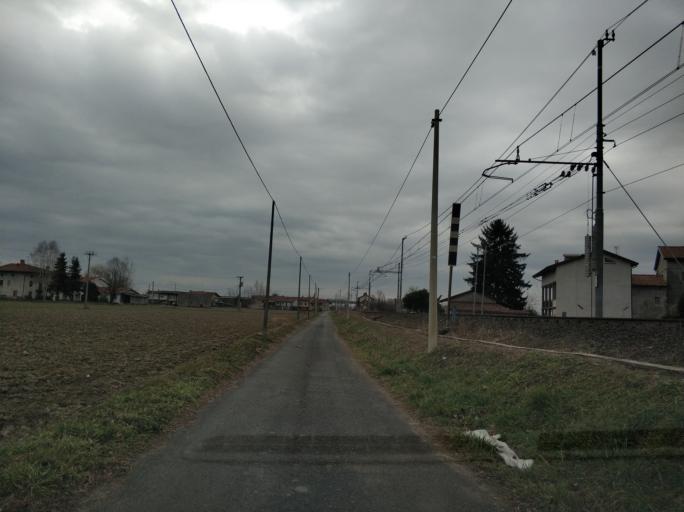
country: IT
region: Piedmont
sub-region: Provincia di Torino
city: Ivrea
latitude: 45.4485
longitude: 7.8845
